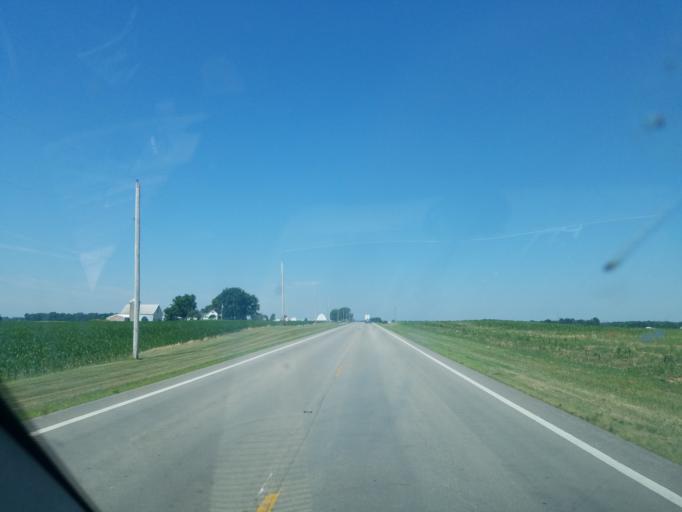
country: US
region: Ohio
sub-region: Shelby County
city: Botkins
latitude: 40.4386
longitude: -84.2261
